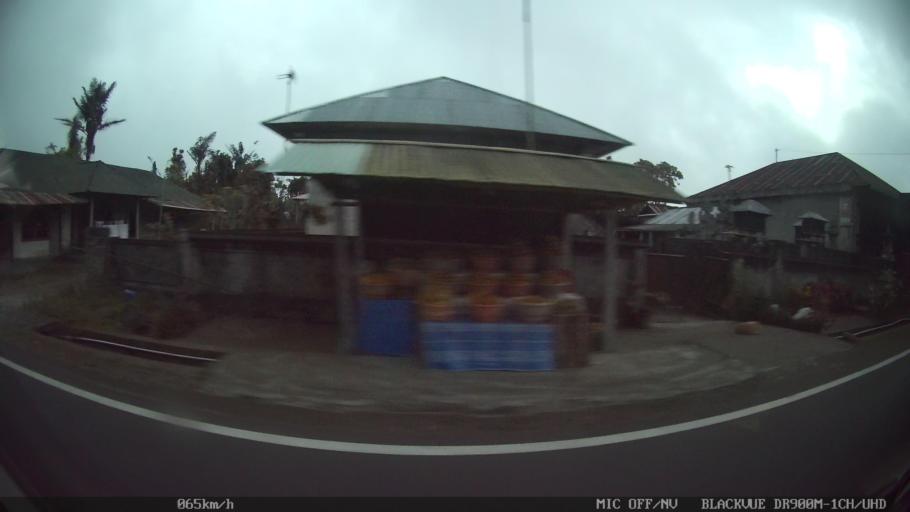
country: ID
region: Bali
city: Banjar Kedisan
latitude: -8.2851
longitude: 115.3201
